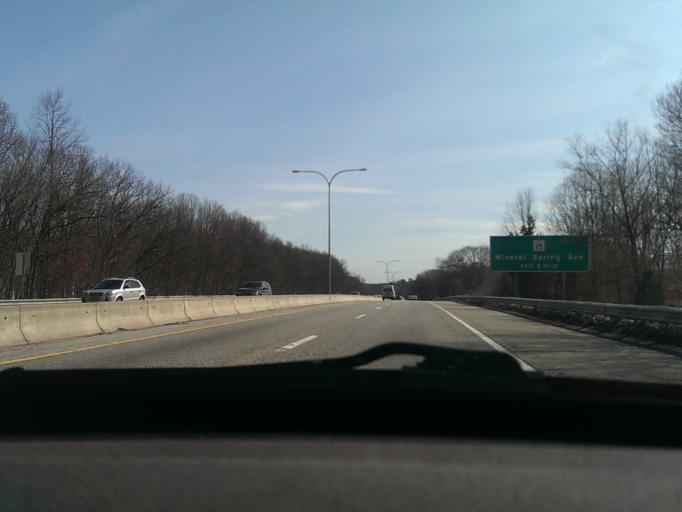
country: US
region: Rhode Island
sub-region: Providence County
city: North Providence
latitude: 41.8826
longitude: -71.4363
